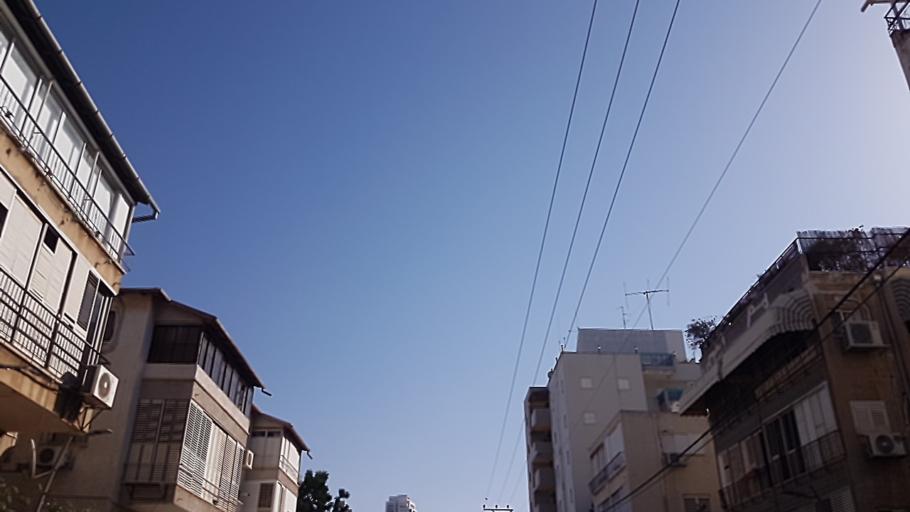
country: IL
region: Tel Aviv
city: Bene Beraq
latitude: 32.0771
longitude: 34.8232
